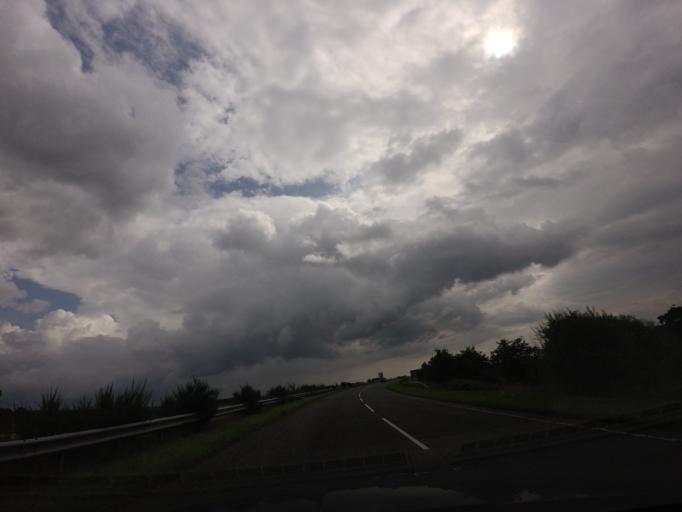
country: GB
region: Scotland
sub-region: Dumfries and Galloway
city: Lockerbie
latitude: 55.1064
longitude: -3.3483
